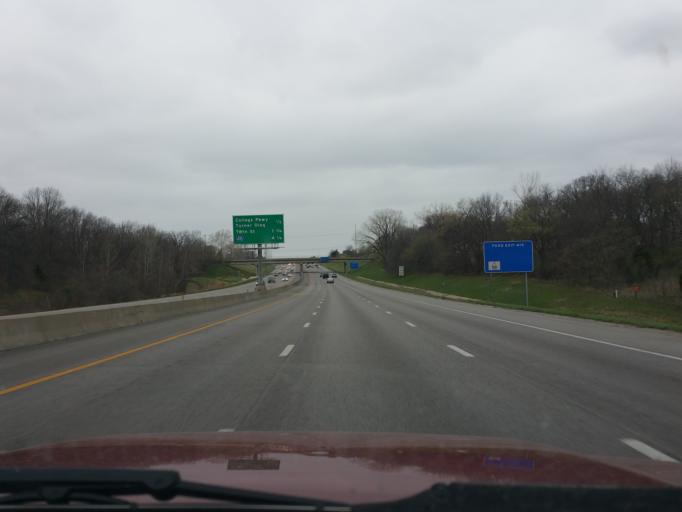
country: US
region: Kansas
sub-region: Johnson County
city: Shawnee
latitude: 39.1060
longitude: -94.7239
